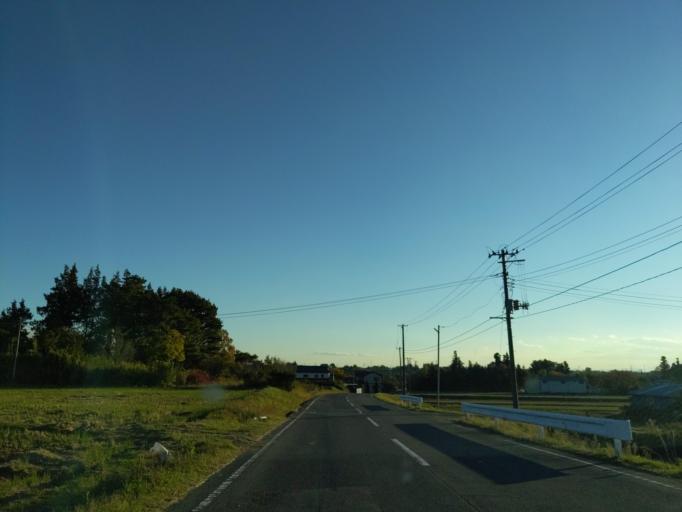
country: JP
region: Fukushima
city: Koriyama
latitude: 37.4507
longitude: 140.3711
